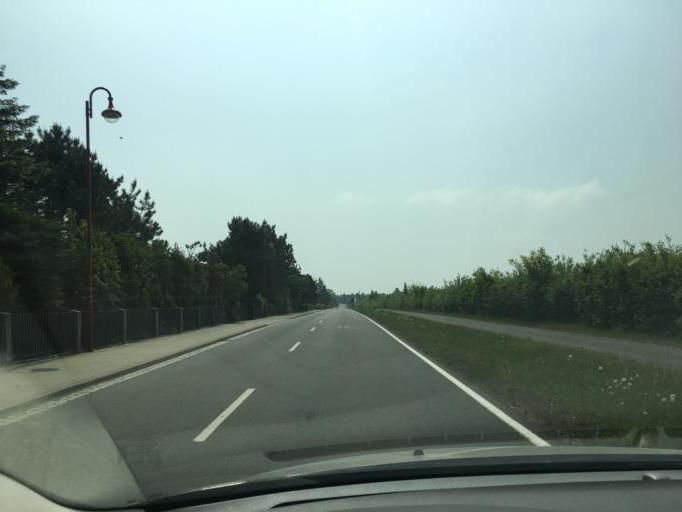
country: DE
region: Saxony
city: Grossposna
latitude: 51.2813
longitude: 12.5045
